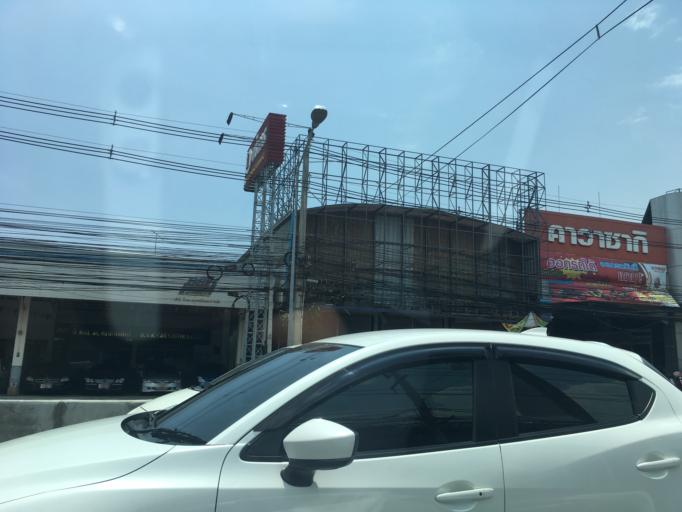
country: TH
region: Chon Buri
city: Chon Buri
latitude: 13.3499
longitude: 100.9802
